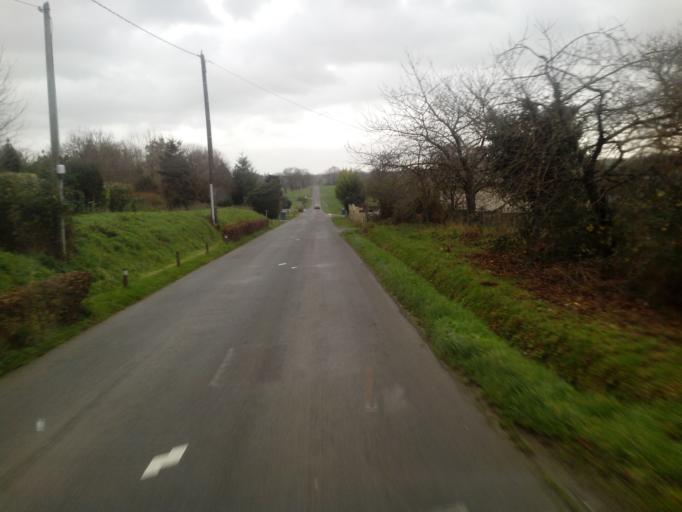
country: FR
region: Brittany
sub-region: Departement d'Ille-et-Vilaine
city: Saint-Medard-sur-Ille
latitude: 48.2482
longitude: -1.6472
